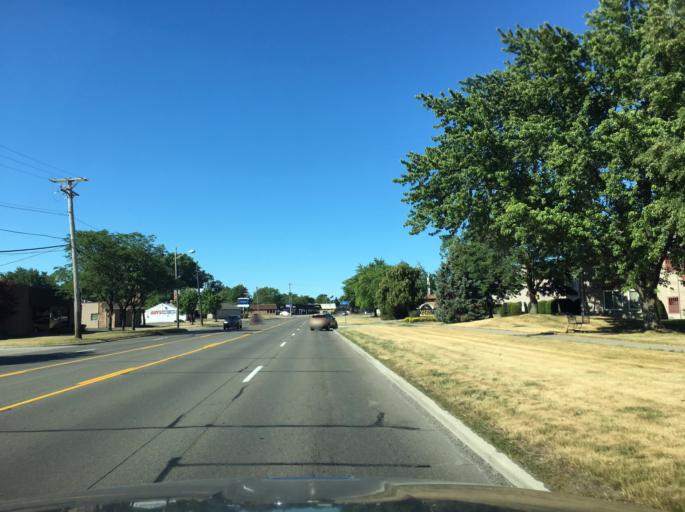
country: US
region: Michigan
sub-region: Macomb County
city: Saint Clair Shores
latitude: 42.5296
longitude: -82.8906
